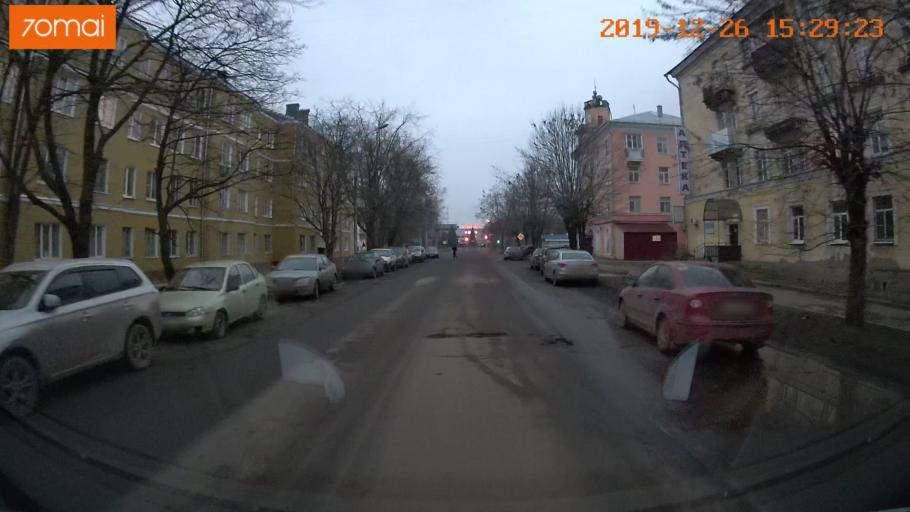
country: RU
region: Jaroslavl
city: Rybinsk
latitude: 58.0571
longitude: 38.8168
